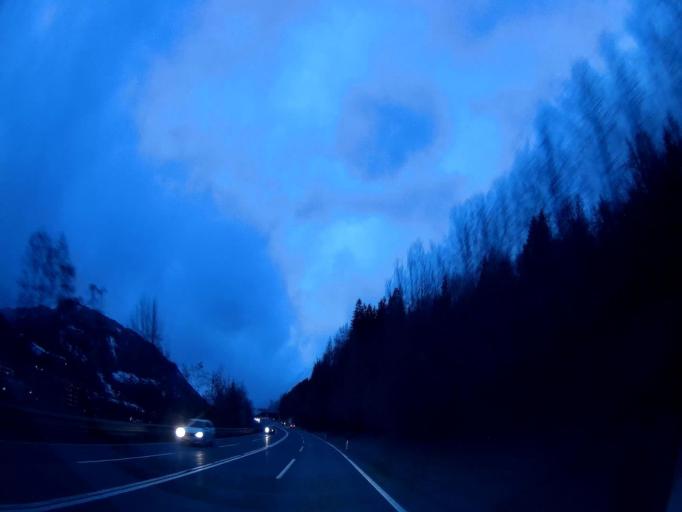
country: AT
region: Salzburg
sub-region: Politischer Bezirk Sankt Johann im Pongau
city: Bischofshofen
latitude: 47.4003
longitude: 13.2268
